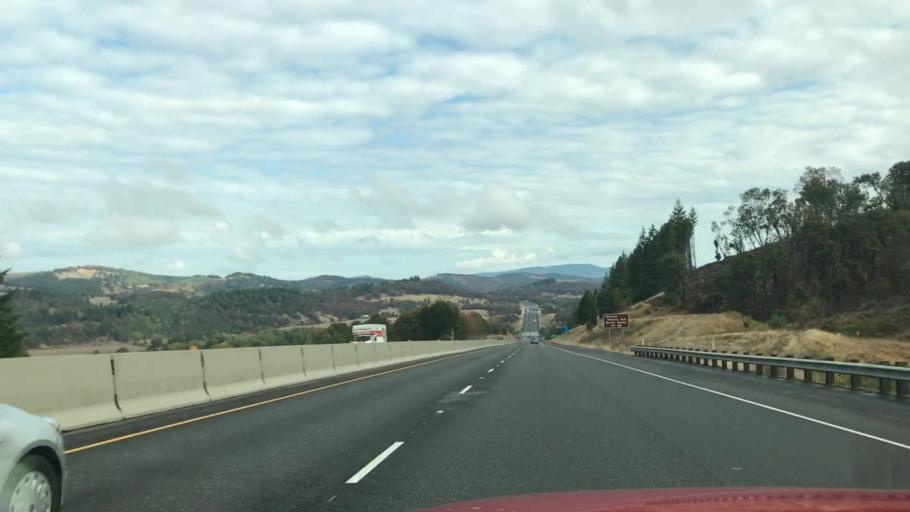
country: US
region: Oregon
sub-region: Douglas County
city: Sutherlin
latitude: 43.4056
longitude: -123.3334
